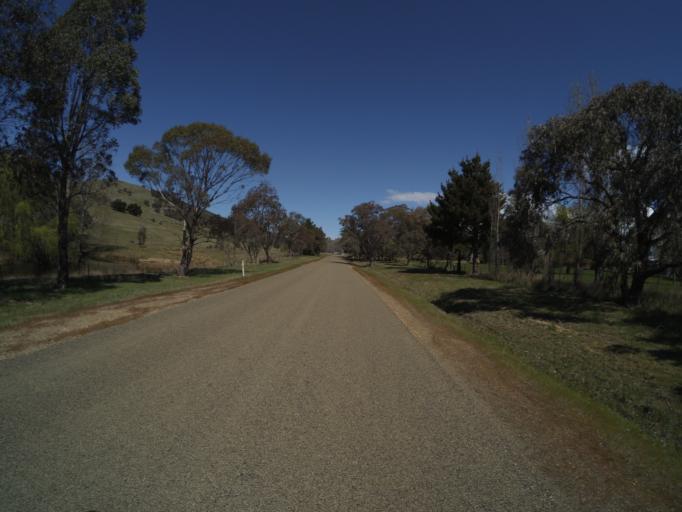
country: AU
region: Australian Capital Territory
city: Macquarie
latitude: -35.1545
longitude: 148.8846
